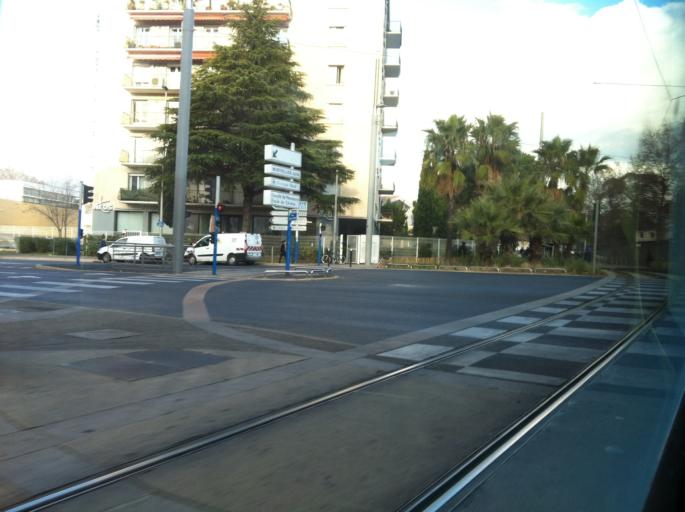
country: FR
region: Languedoc-Roussillon
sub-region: Departement de l'Herault
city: Montpellier
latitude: 43.6262
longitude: 3.8664
